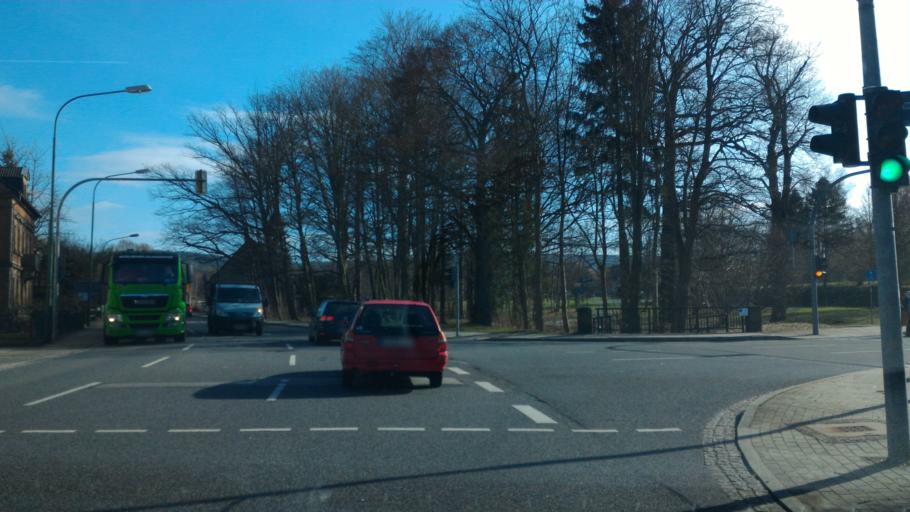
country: DE
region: Saxony
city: Neustadt in Sachsen
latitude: 51.0246
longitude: 14.2199
